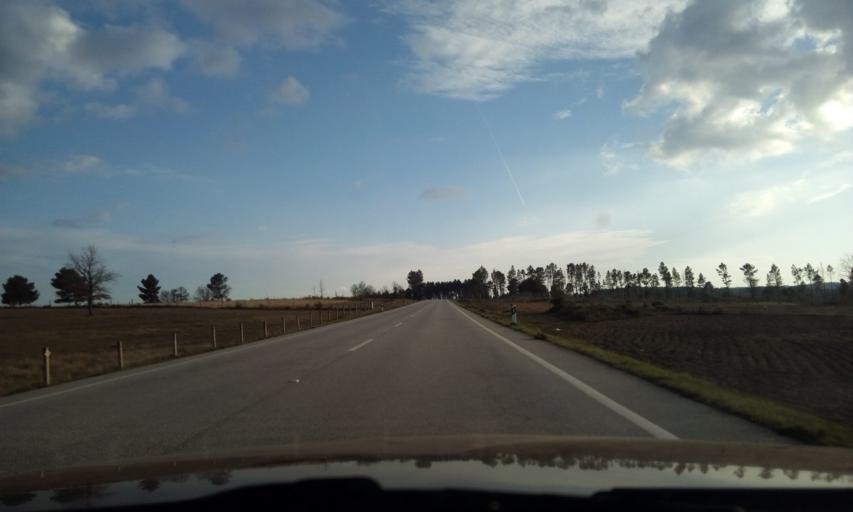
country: PT
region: Guarda
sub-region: Pinhel
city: Pinhel
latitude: 40.6468
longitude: -6.9680
